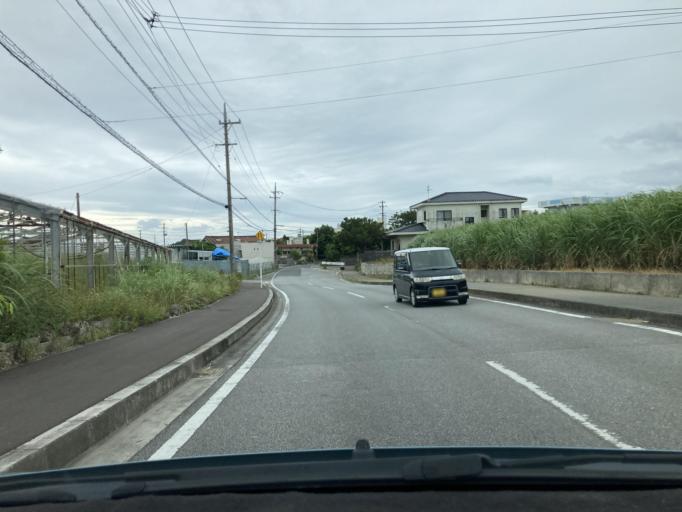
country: JP
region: Okinawa
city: Itoman
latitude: 26.1490
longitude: 127.6940
